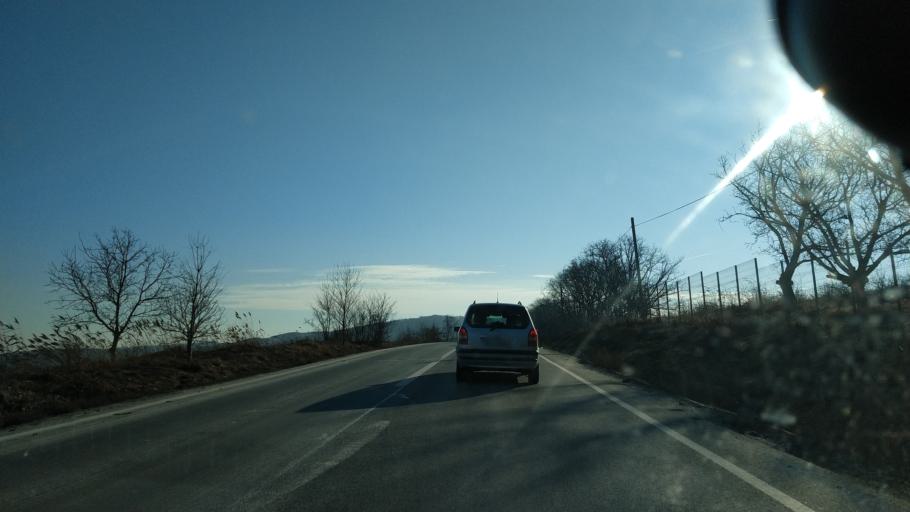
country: RO
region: Iasi
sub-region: Comuna Strunga
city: Strunga
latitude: 47.1747
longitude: 26.9540
